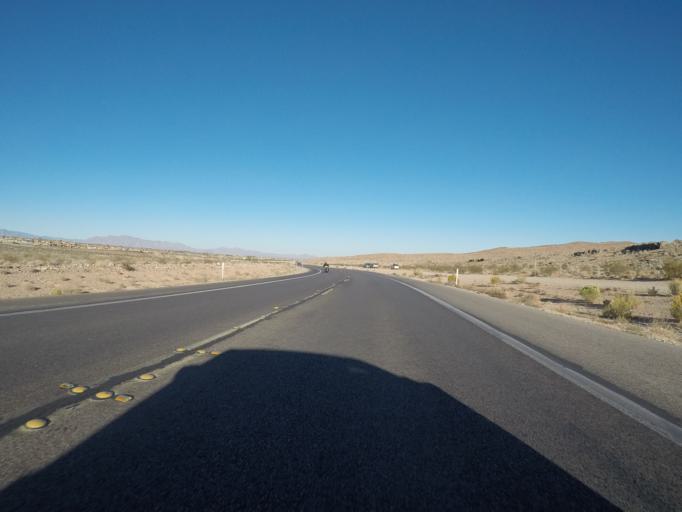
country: US
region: Nevada
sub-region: Clark County
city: Summerlin South
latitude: 36.1496
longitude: -115.3725
